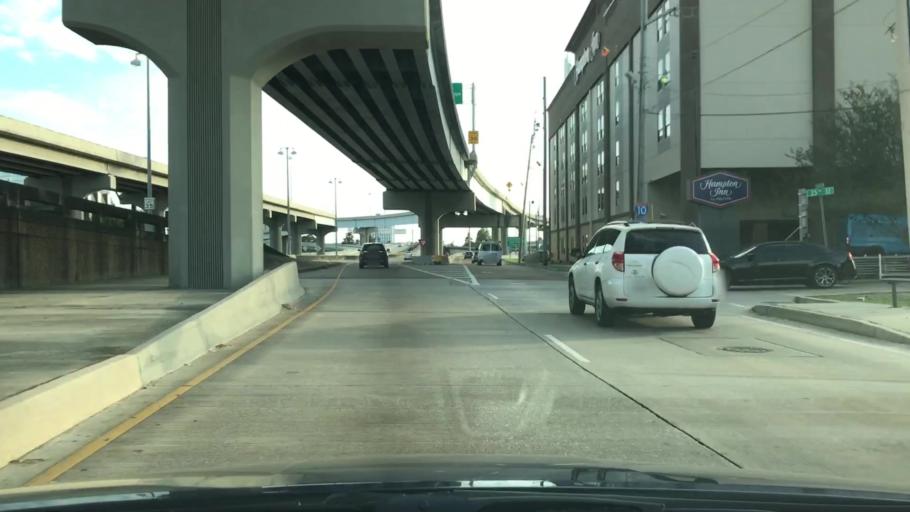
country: US
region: Louisiana
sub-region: Jefferson Parish
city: Metairie
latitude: 30.0023
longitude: -90.1555
